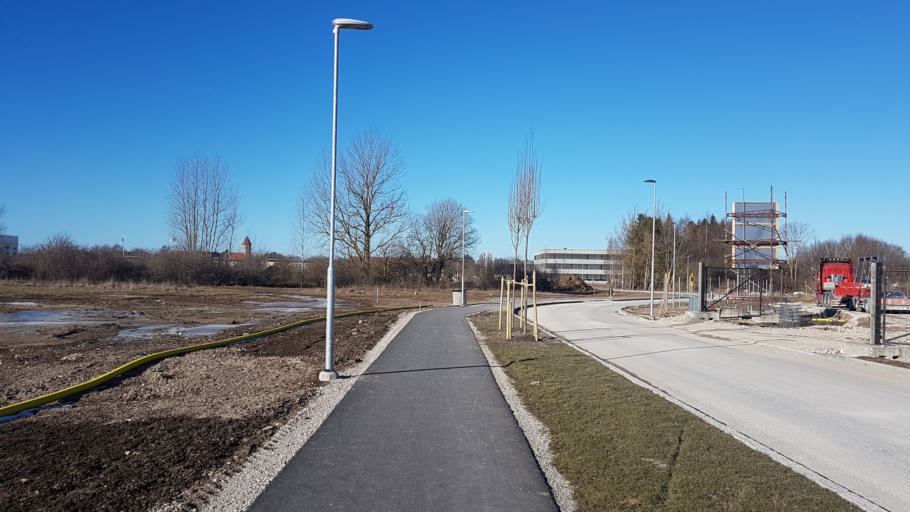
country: SE
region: Gotland
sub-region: Gotland
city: Visby
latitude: 57.6280
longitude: 18.3092
